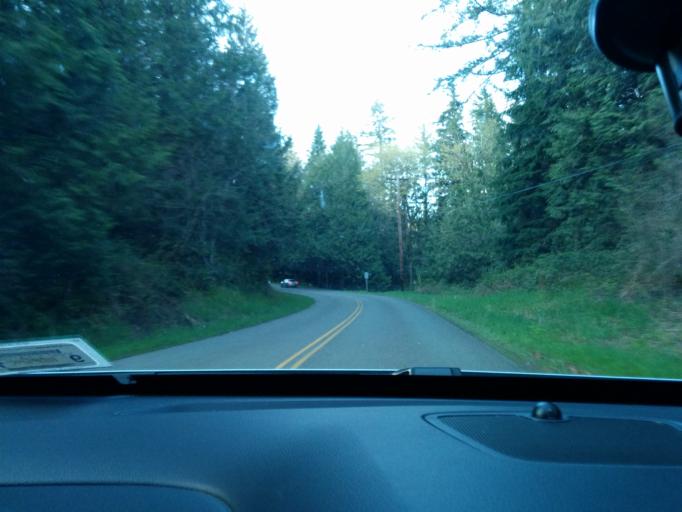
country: US
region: Washington
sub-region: Snohomish County
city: Gold Bar
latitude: 47.8868
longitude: -121.7351
